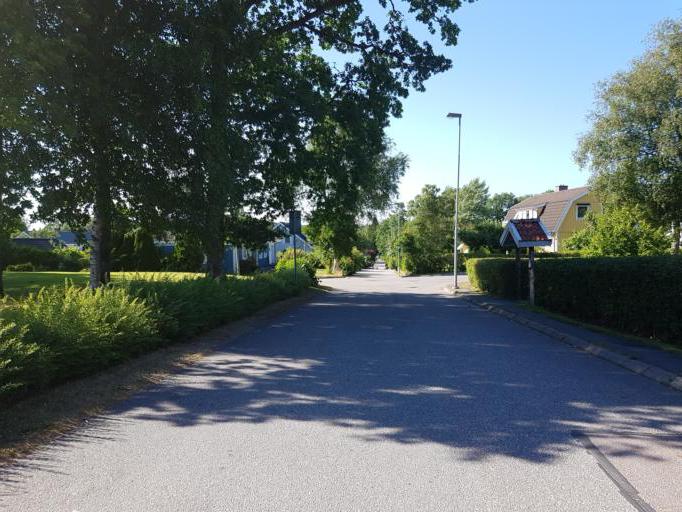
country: SE
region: Vaestra Goetaland
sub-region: Partille Kommun
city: Furulund
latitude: 57.7054
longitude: 12.1439
